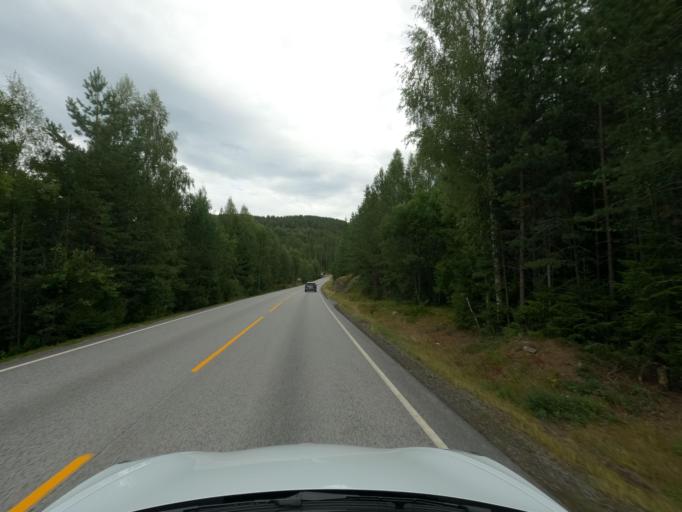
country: NO
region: Telemark
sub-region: Hjartdal
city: Sauland
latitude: 59.6911
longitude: 9.0226
